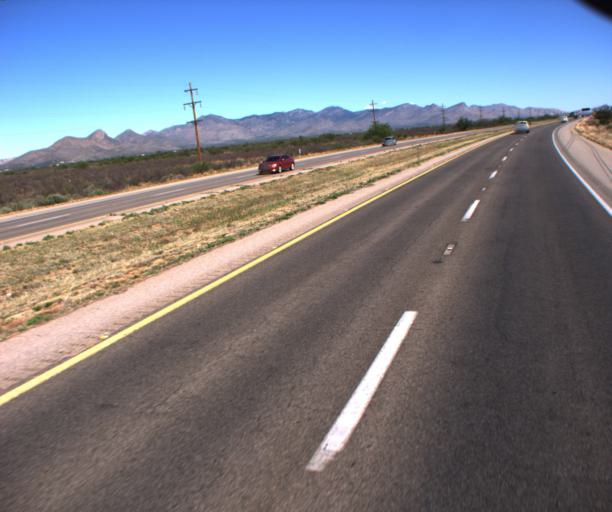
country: US
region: Arizona
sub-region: Cochise County
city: Huachuca City
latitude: 31.6634
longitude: -110.3501
